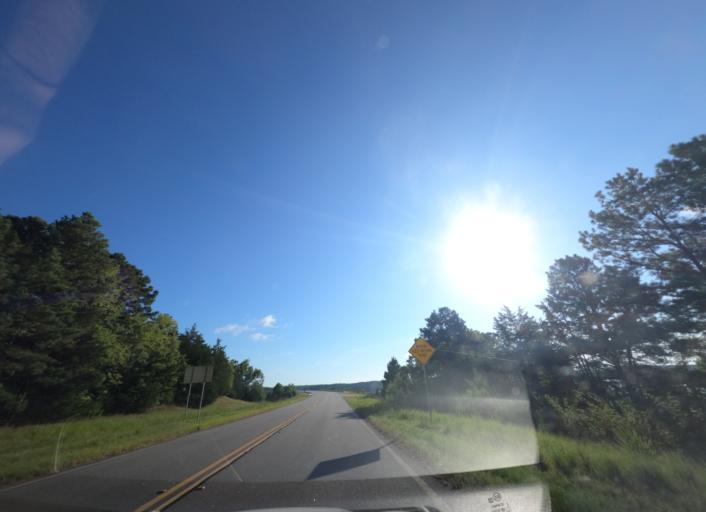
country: US
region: Georgia
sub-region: Lincoln County
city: Lincolnton
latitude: 33.8529
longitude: -82.3932
